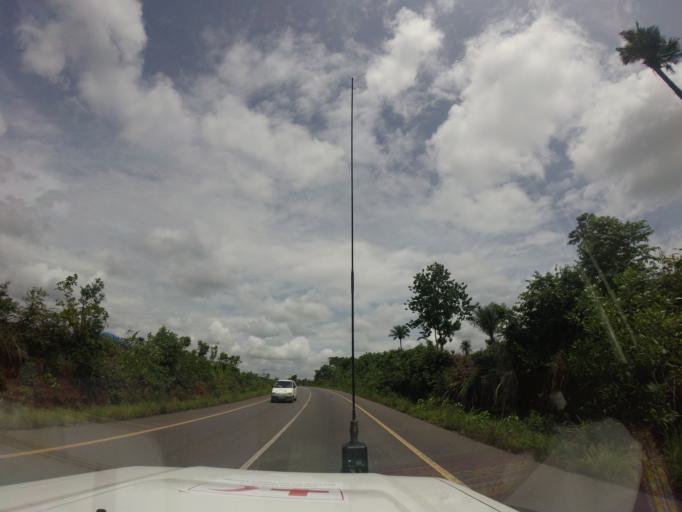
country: SL
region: Northern Province
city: Port Loko
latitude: 8.7529
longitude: -12.7718
